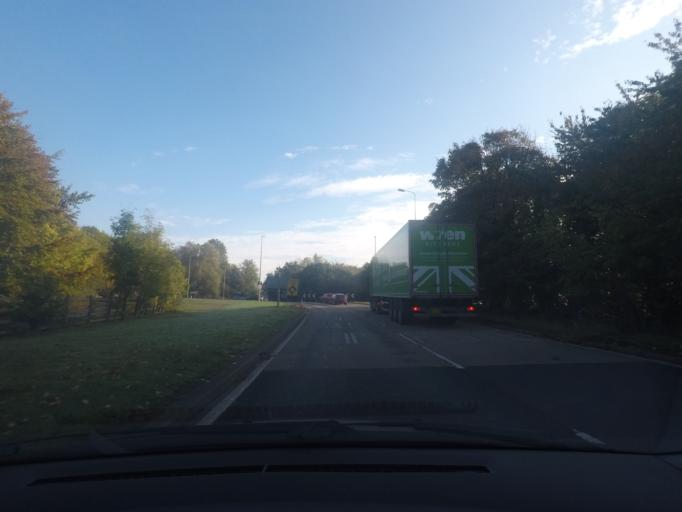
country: GB
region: England
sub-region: East Riding of Yorkshire
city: Hessle
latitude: 53.7217
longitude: -0.4649
